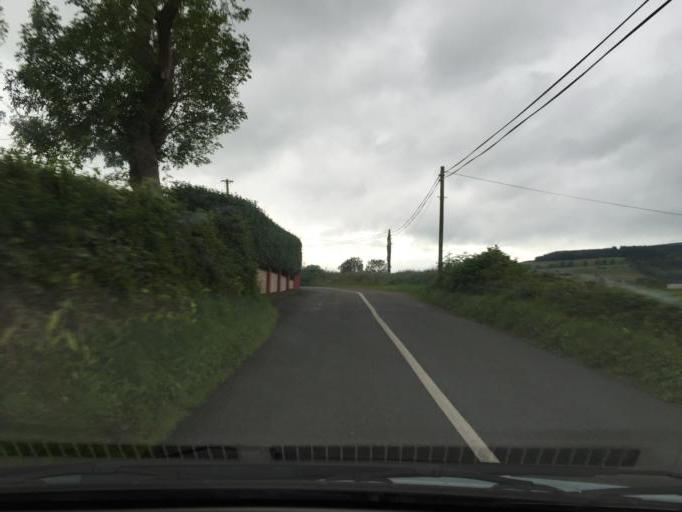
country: IE
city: Ballisodare
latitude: 54.2613
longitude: -8.5296
